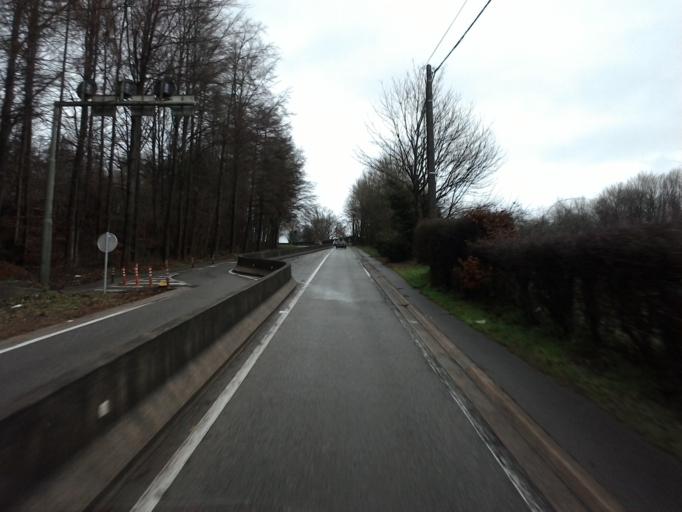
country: BE
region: Wallonia
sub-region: Province de Liege
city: Stavelot
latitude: 50.4003
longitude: 5.9335
